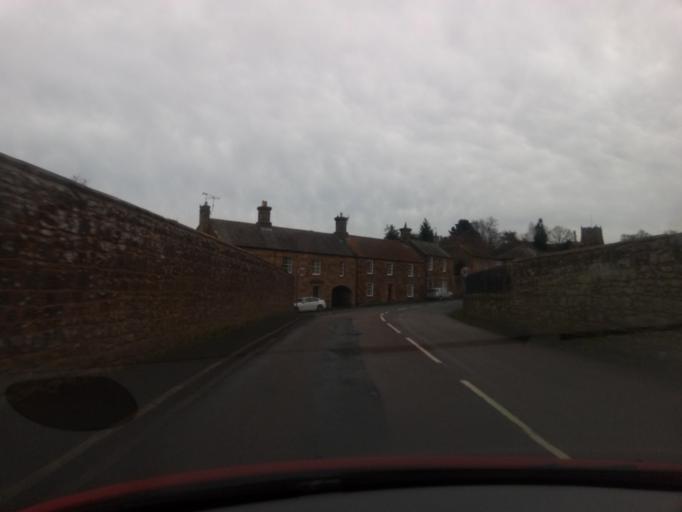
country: GB
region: England
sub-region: Northumberland
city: Alnwick
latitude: 55.4189
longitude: -1.7136
